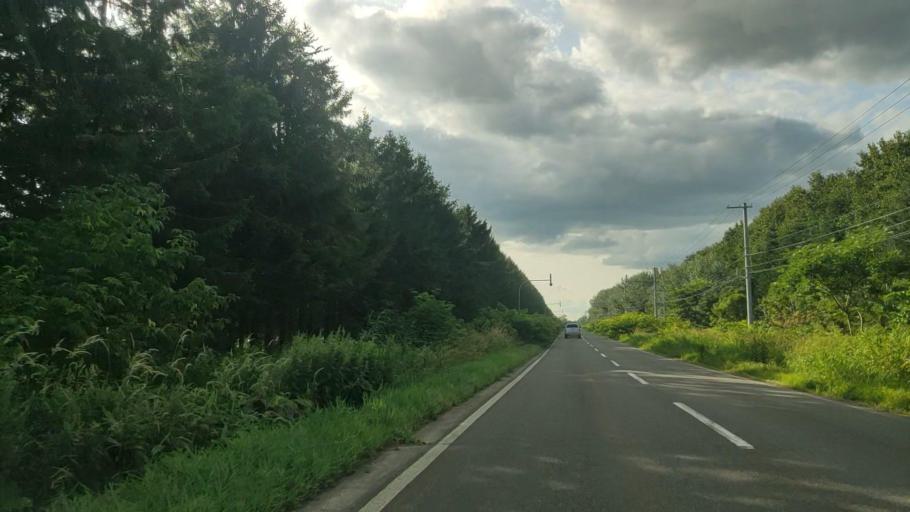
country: JP
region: Hokkaido
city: Makubetsu
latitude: 44.8992
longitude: 141.9138
